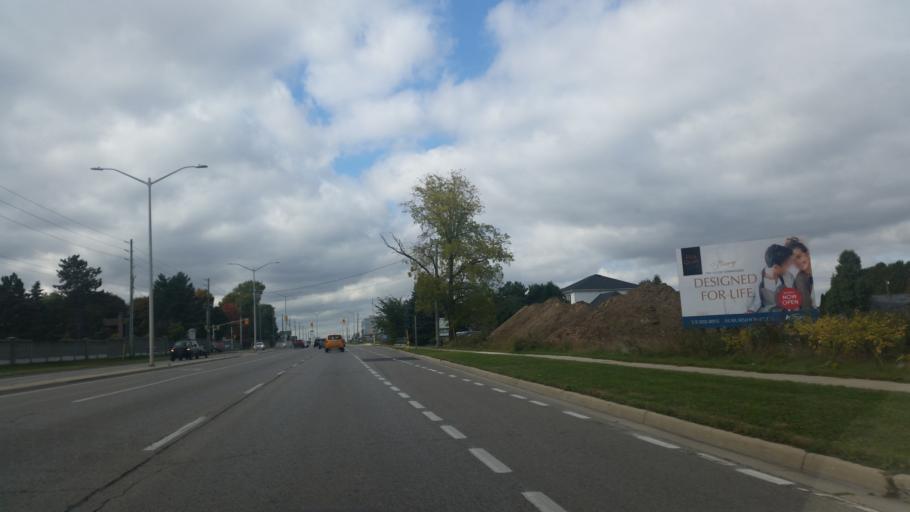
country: CA
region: Ontario
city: London
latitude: 43.0158
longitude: -81.3200
